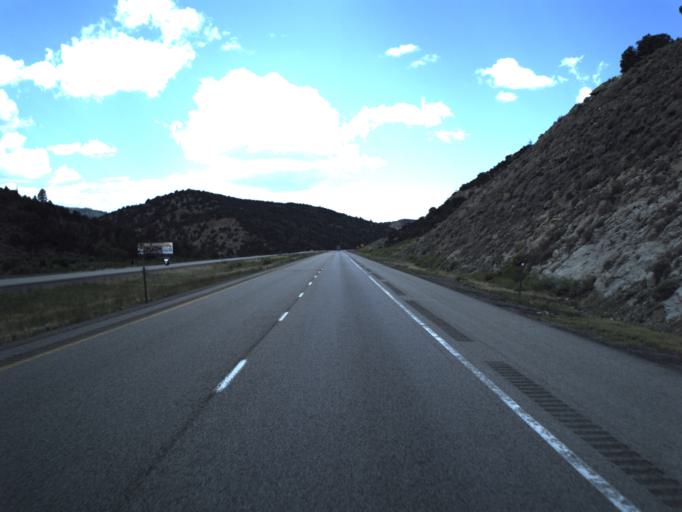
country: US
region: Utah
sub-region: Wayne County
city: Loa
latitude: 38.7602
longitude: -111.4532
